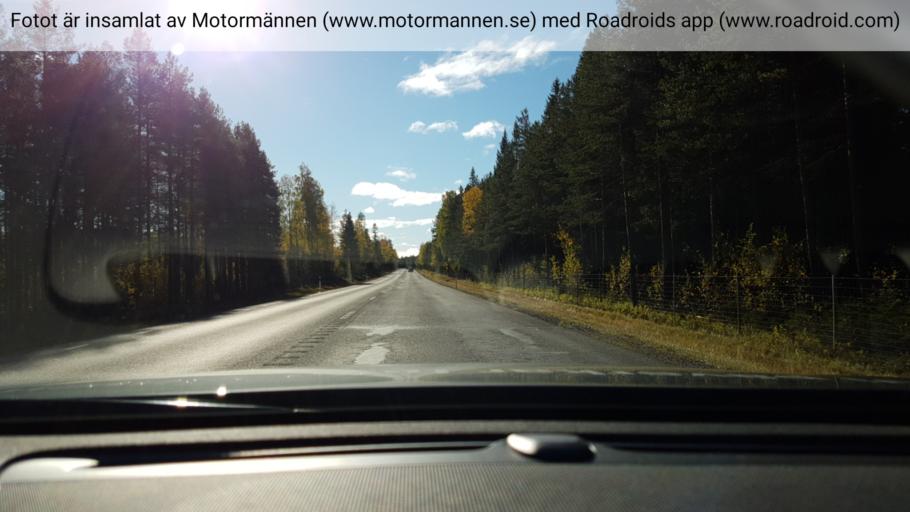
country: SE
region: Vaesterbotten
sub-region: Skelleftea Kommun
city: Burea
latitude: 64.5762
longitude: 21.2234
